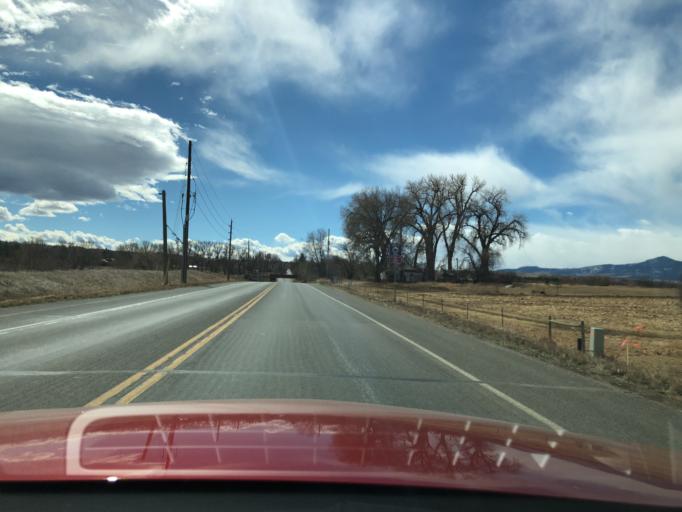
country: US
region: Colorado
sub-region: Boulder County
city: Gunbarrel
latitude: 40.0122
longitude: -105.1783
